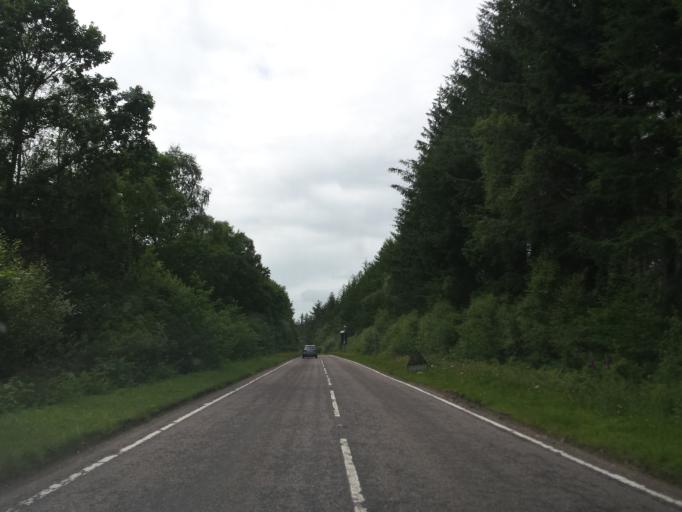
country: GB
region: Scotland
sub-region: Highland
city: Fort William
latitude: 56.8555
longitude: -5.1933
